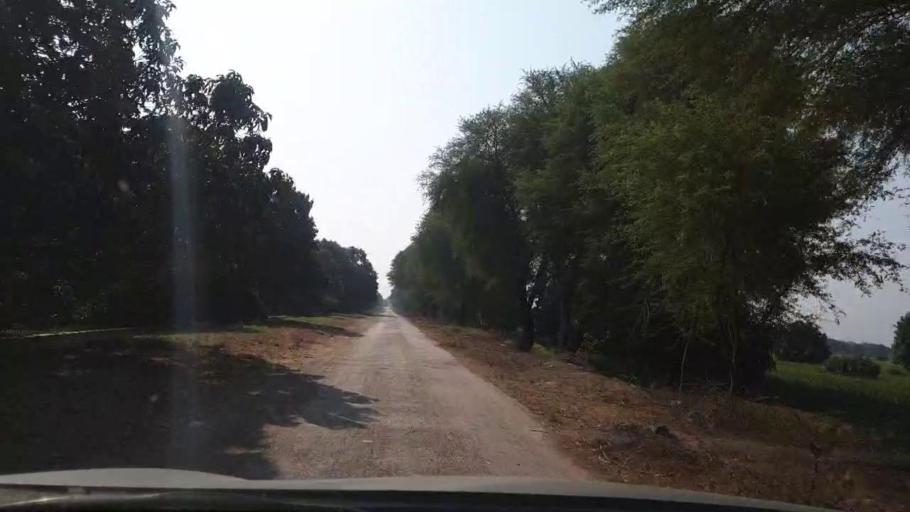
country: PK
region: Sindh
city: Tando Allahyar
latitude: 25.5150
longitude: 68.7861
